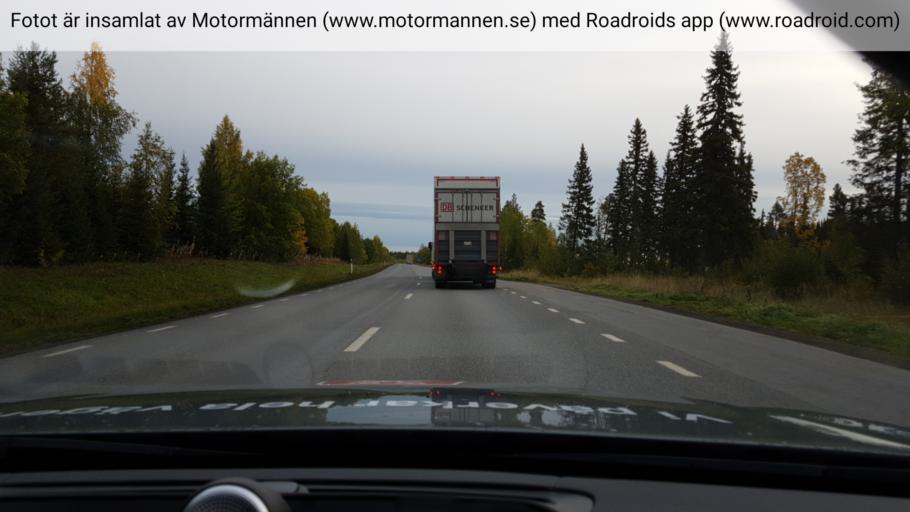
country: SE
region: Jaemtland
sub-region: Stroemsunds Kommun
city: Stroemsund
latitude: 63.5093
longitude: 15.2816
